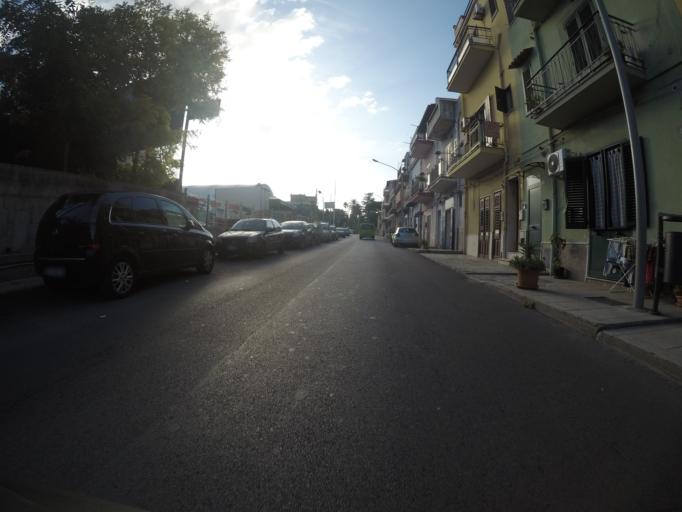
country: IT
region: Sicily
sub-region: Palermo
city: Isola delle Femmine
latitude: 38.1968
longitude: 13.2781
